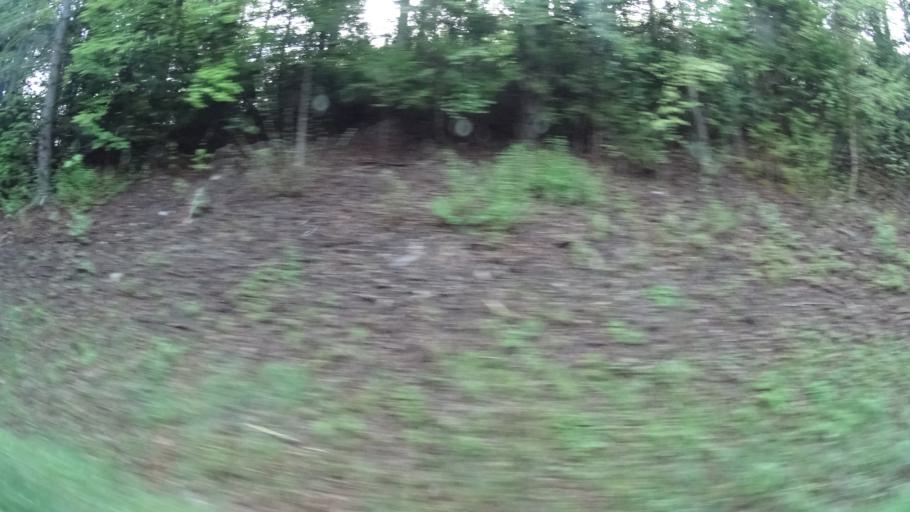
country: DE
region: Baden-Wuerttemberg
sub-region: Karlsruhe Region
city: Empfingen
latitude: 48.4360
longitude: 8.7708
